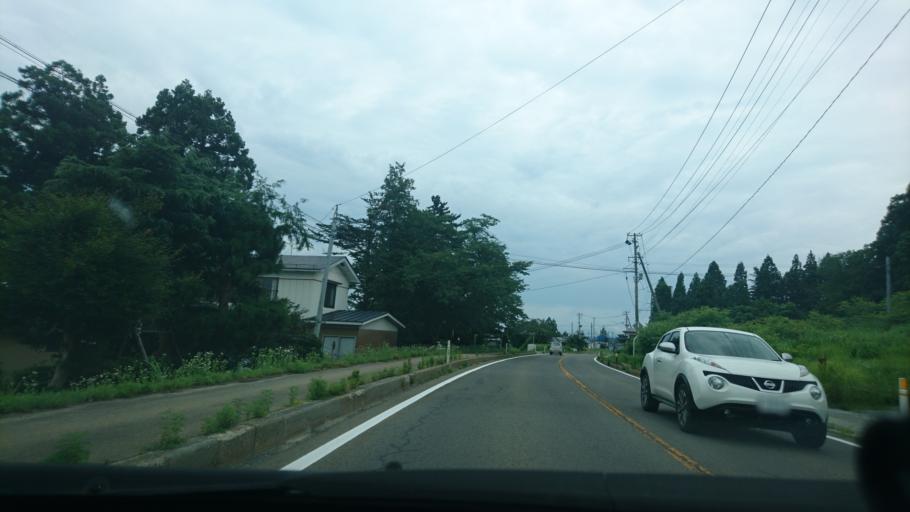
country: JP
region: Akita
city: Yokotemachi
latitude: 39.3561
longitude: 140.5623
